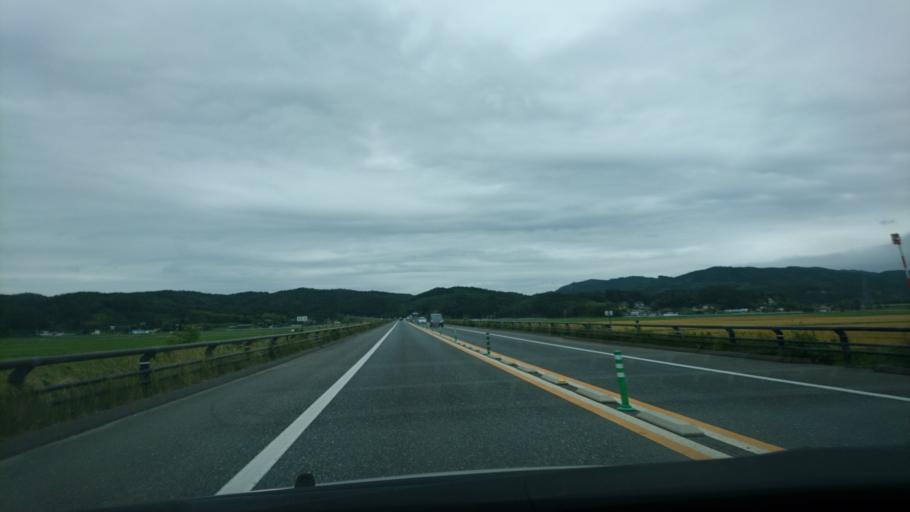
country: JP
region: Miyagi
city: Wakuya
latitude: 38.6121
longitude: 141.2843
